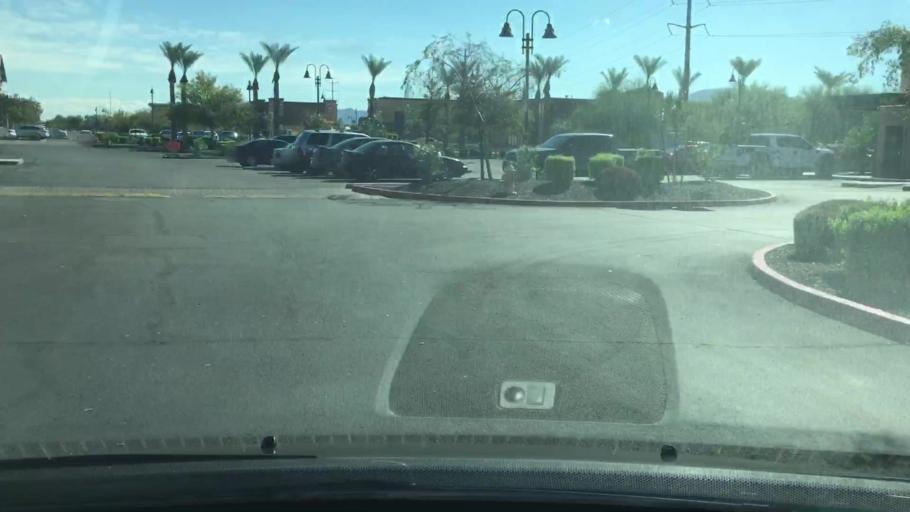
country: US
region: Arizona
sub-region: Maricopa County
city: Laveen
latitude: 33.3787
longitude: -112.1366
